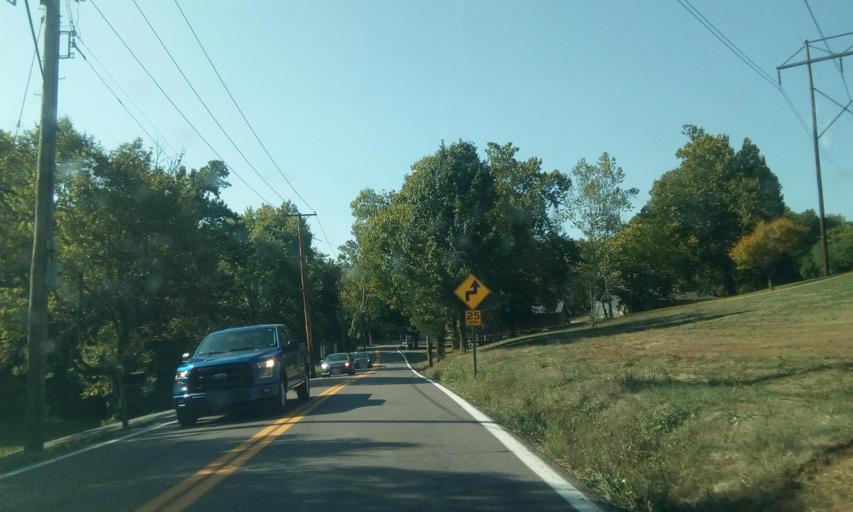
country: US
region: Missouri
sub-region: Saint Louis County
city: Mehlville
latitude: 38.4977
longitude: -90.3460
